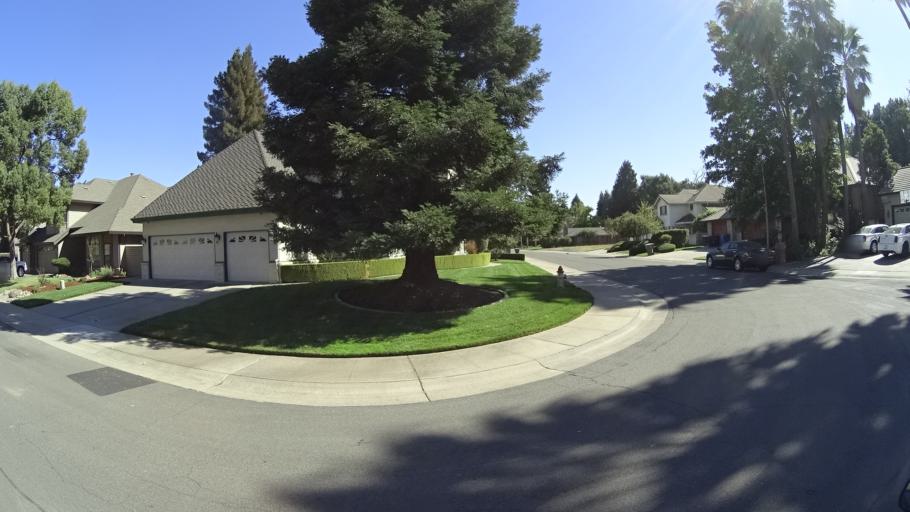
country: US
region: California
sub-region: Sacramento County
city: Parkway
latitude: 38.4778
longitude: -121.5410
